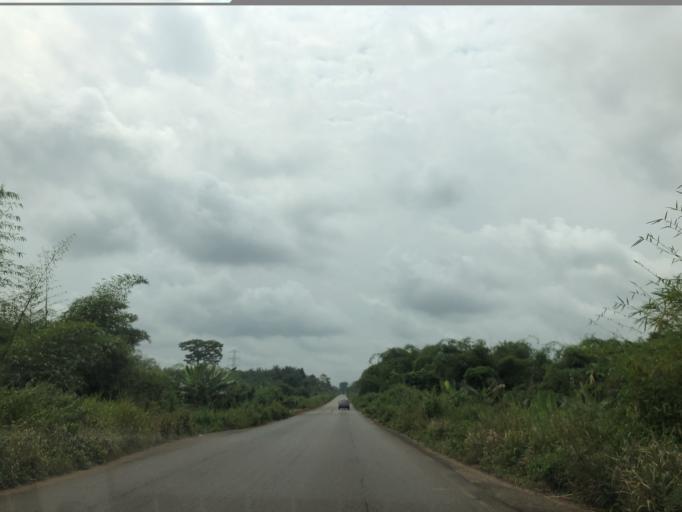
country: CM
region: Littoral
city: Edea
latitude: 3.7063
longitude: 10.1070
